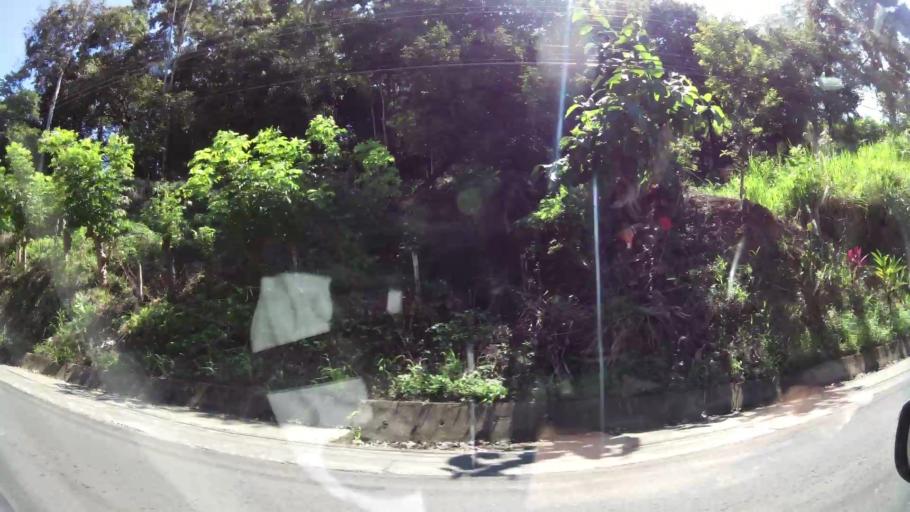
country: CR
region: Puntarenas
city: Quepos
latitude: 9.4316
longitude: -84.1588
